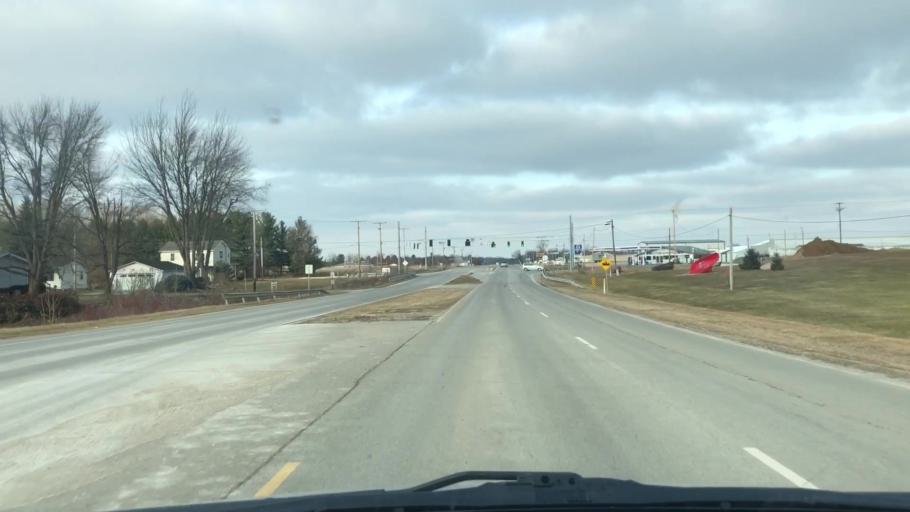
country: US
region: Indiana
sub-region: Steuben County
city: Angola
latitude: 41.6700
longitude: -85.0286
